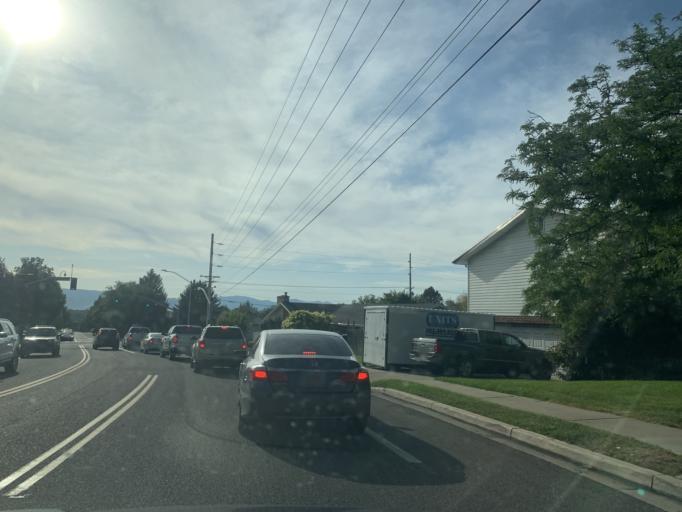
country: US
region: Utah
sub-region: Utah County
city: Provo
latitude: 40.2632
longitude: -111.6466
